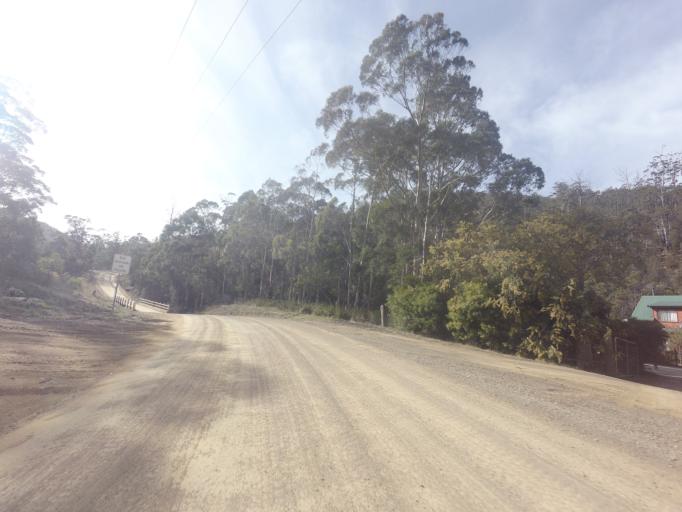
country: AU
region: Tasmania
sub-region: Huon Valley
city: Huonville
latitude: -43.0633
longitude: 147.0928
